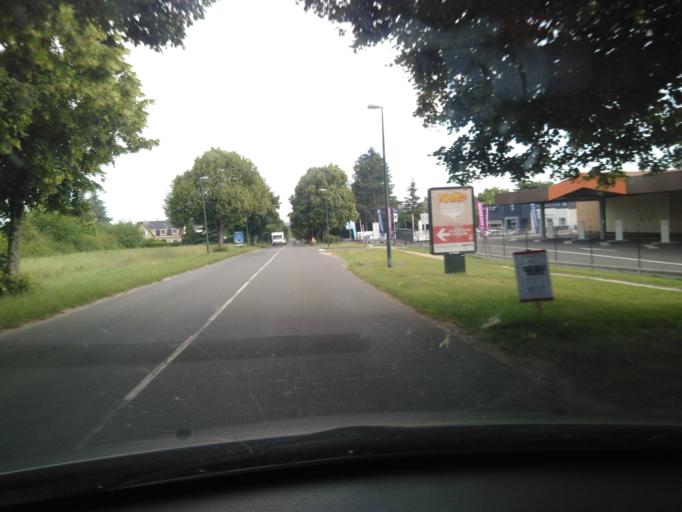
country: FR
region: Centre
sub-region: Departement d'Indre-et-Loire
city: Amboise
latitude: 47.3985
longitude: 0.9798
